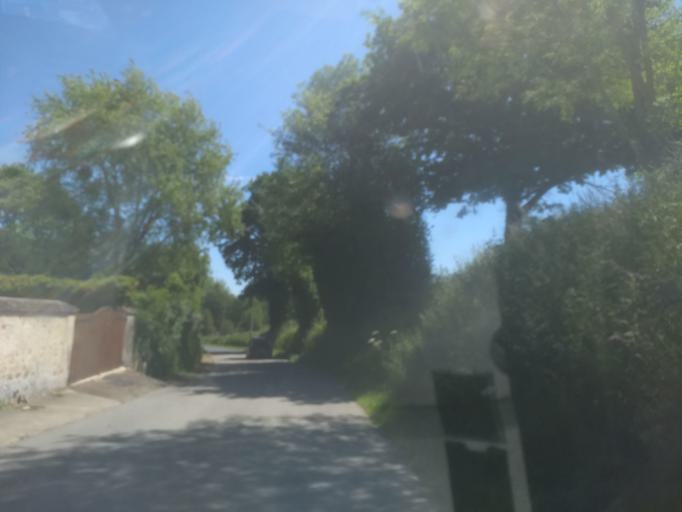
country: FR
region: Lower Normandy
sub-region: Departement de l'Orne
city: Remalard
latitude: 48.3622
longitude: 0.7624
